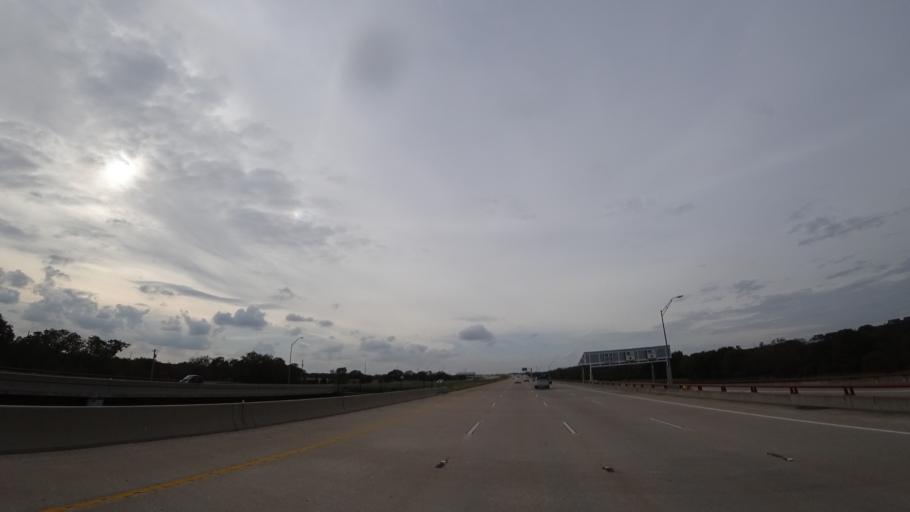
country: US
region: Texas
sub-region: Williamson County
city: Brushy Creek
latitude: 30.4791
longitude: -97.7338
